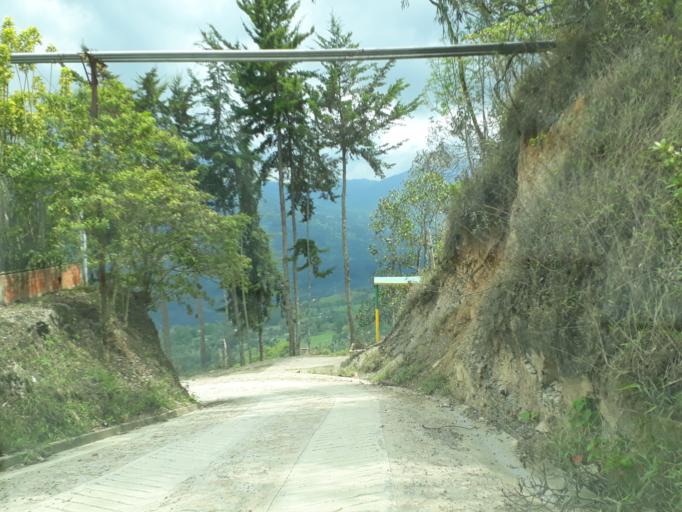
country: CO
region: Cundinamarca
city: Manta
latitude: 5.0128
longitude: -73.5435
